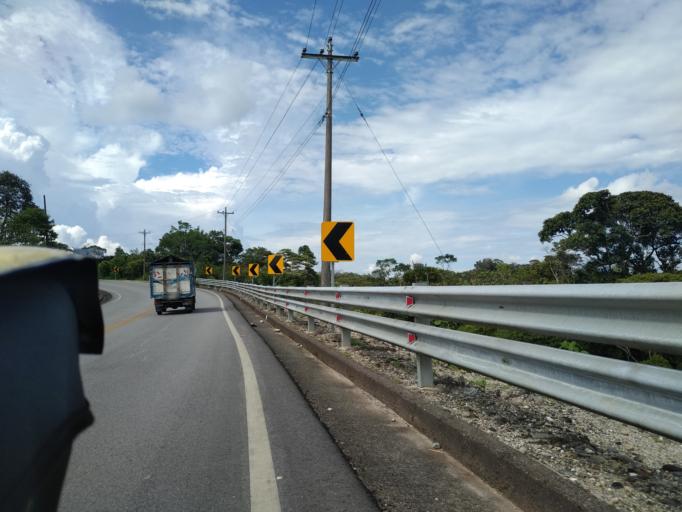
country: EC
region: Napo
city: Tena
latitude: -1.1123
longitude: -77.8064
